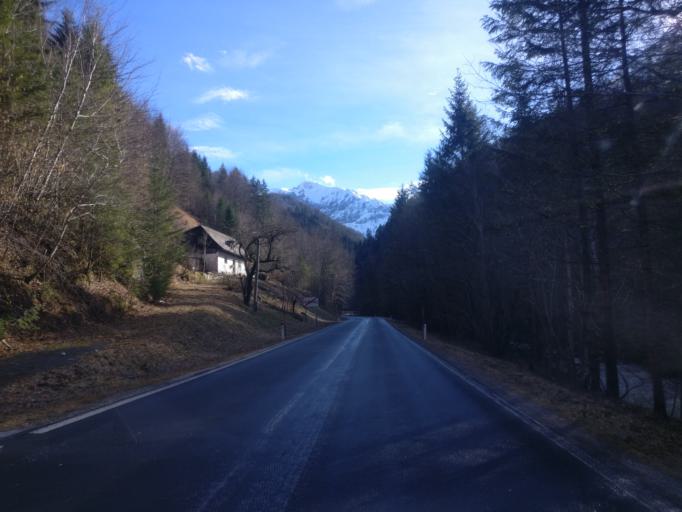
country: AT
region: Styria
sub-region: Politischer Bezirk Liezen
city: Landl
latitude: 47.6625
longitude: 14.7106
